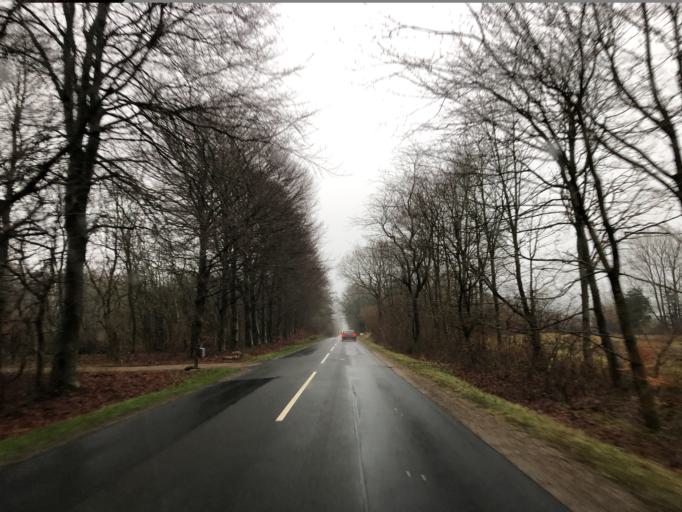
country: DK
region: Central Jutland
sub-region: Holstebro Kommune
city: Ulfborg
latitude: 56.2058
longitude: 8.4054
